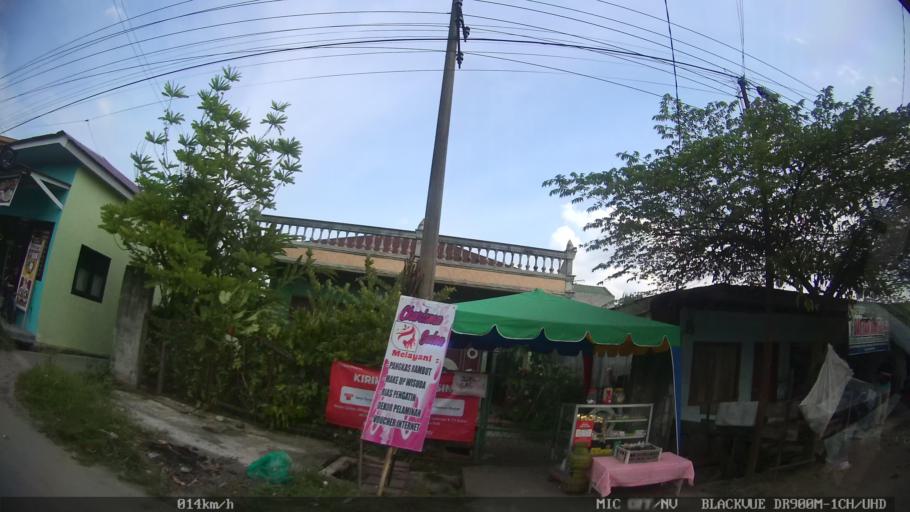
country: ID
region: North Sumatra
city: Binjai
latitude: 3.6375
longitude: 98.4922
